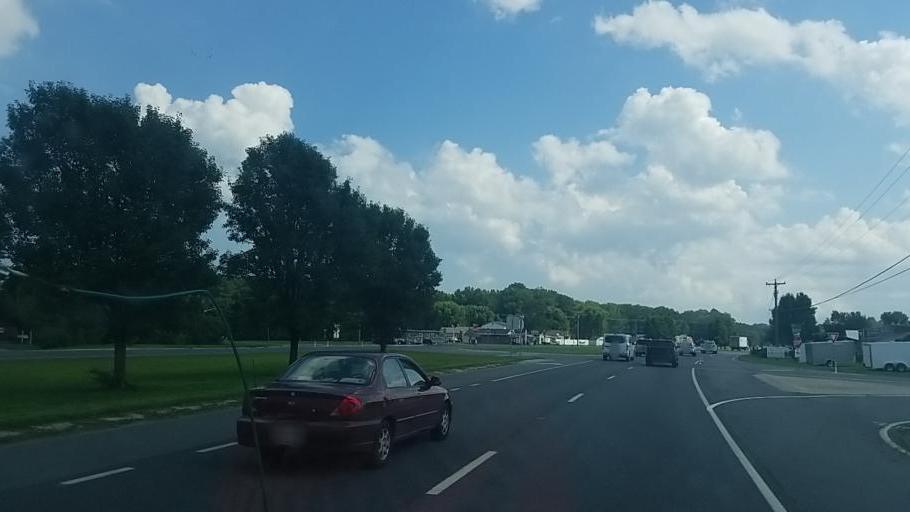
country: US
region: Delaware
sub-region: Sussex County
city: Selbyville
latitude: 38.5155
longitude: -75.2393
